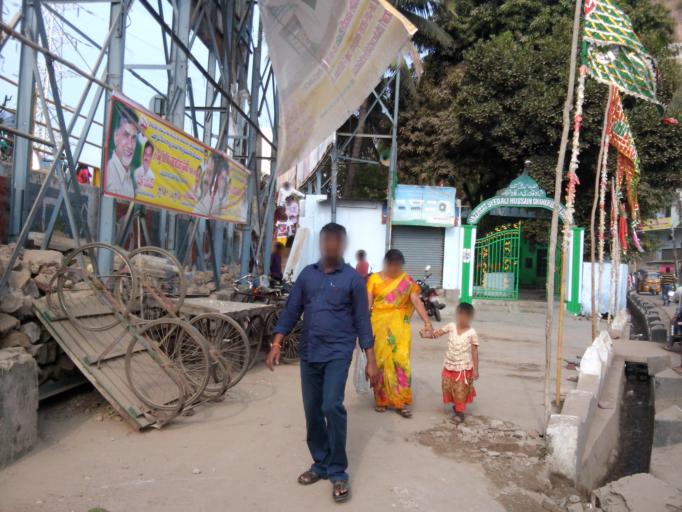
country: IN
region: Andhra Pradesh
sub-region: Krishna
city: Vijayawada
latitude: 16.5124
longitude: 80.6067
